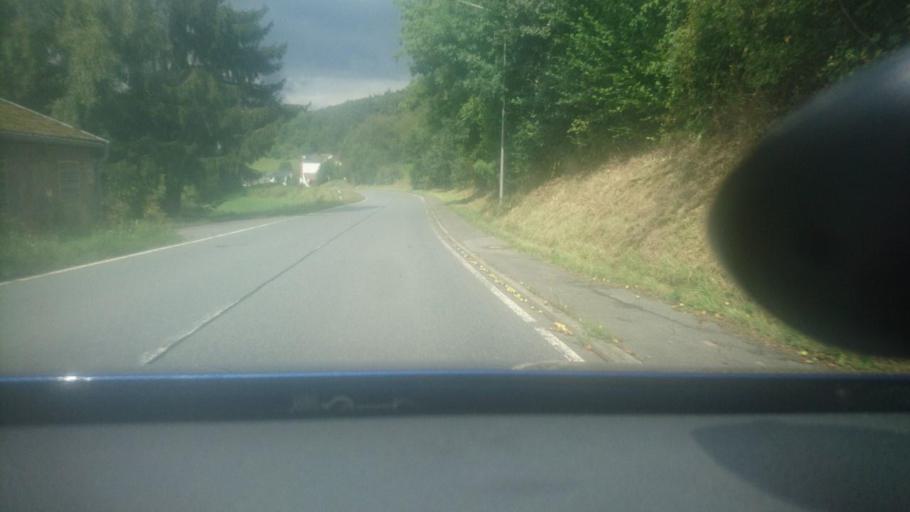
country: DE
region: Hesse
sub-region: Regierungsbezirk Darmstadt
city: Frankisch-Crumbach
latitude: 49.7221
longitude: 8.9081
